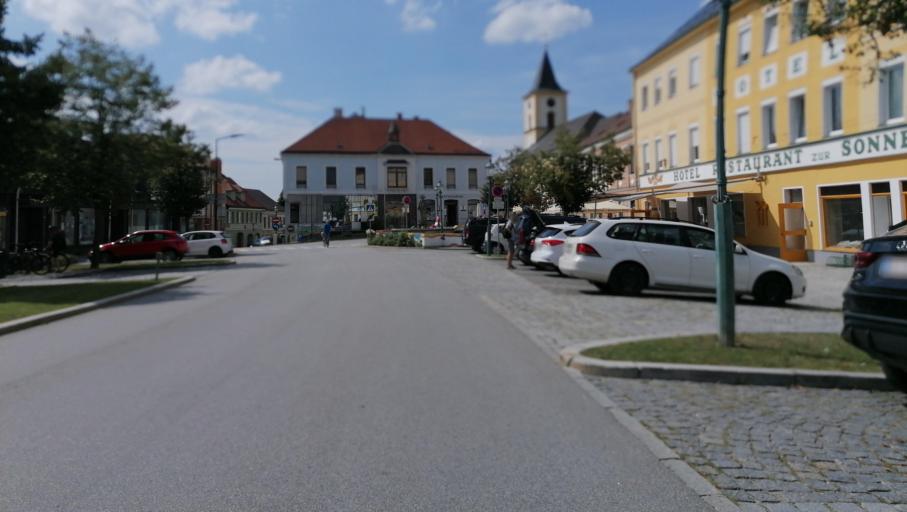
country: AT
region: Lower Austria
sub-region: Politischer Bezirk Gmund
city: Schrems
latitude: 48.7931
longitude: 15.0703
